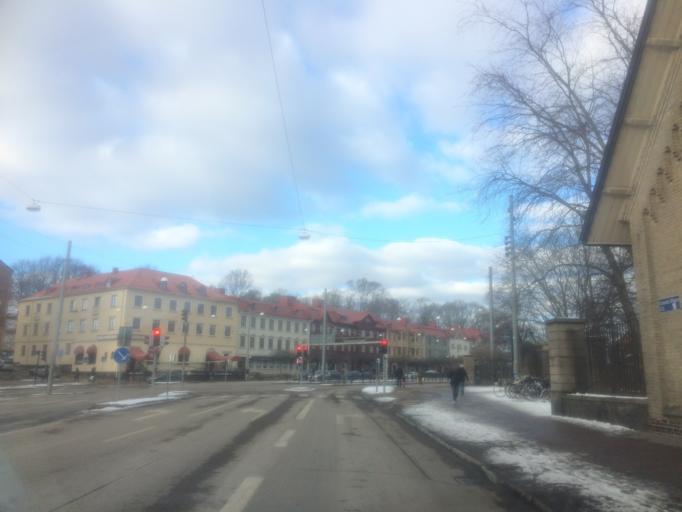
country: SE
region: Vaestra Goetaland
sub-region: Goteborg
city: Goeteborg
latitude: 57.7152
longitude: 12.0046
